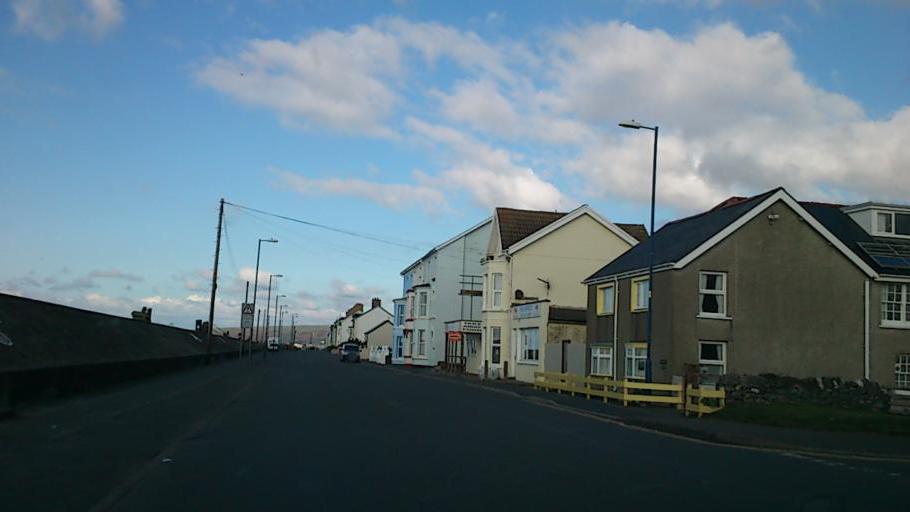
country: GB
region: Wales
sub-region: County of Ceredigion
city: Bow Street
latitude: 52.4930
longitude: -4.0517
